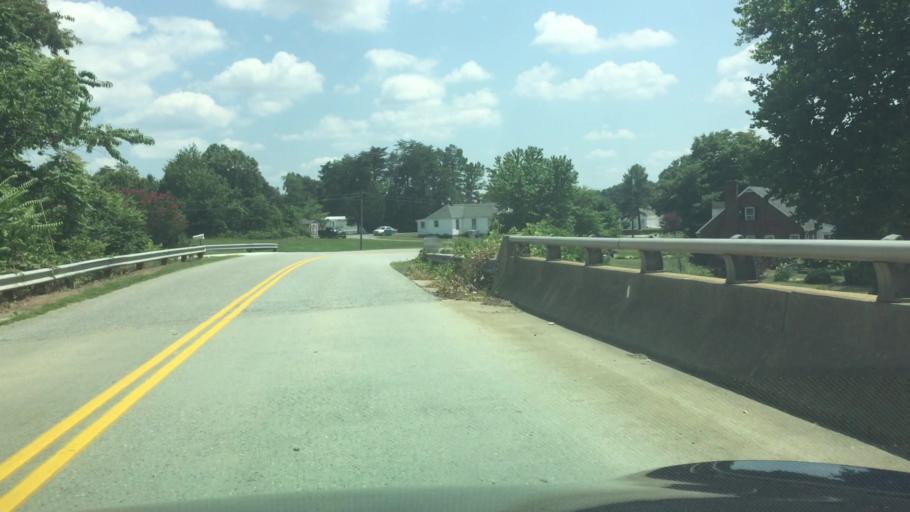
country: US
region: Virginia
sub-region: Campbell County
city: Concord
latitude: 37.3476
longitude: -78.9094
